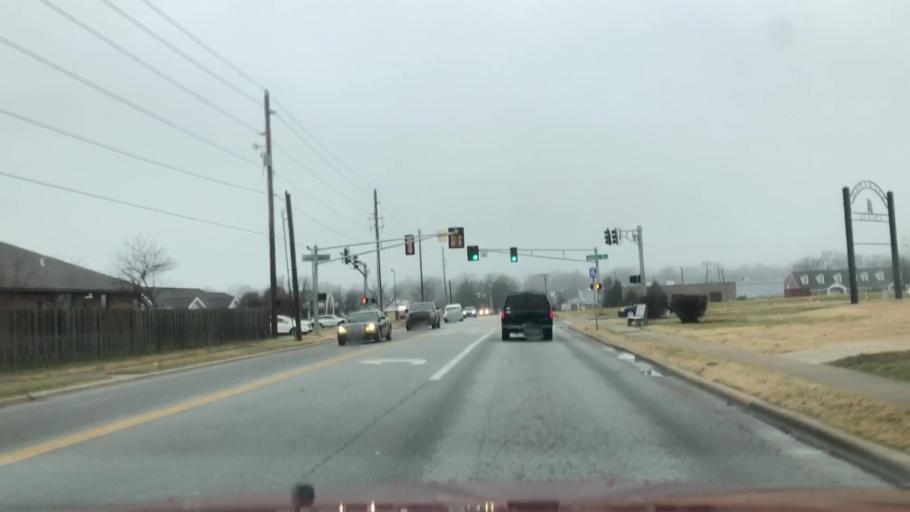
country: US
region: Missouri
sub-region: Greene County
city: Springfield
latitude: 37.1455
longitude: -93.2908
